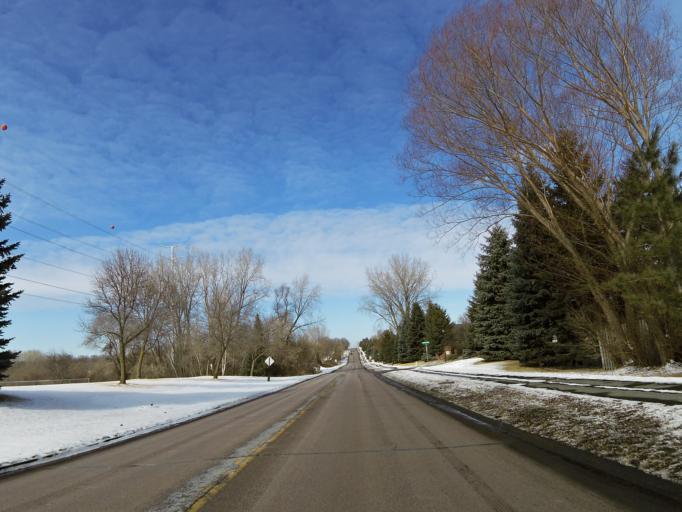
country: US
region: Minnesota
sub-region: Hennepin County
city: Eden Prairie
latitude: 44.8216
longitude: -93.4290
